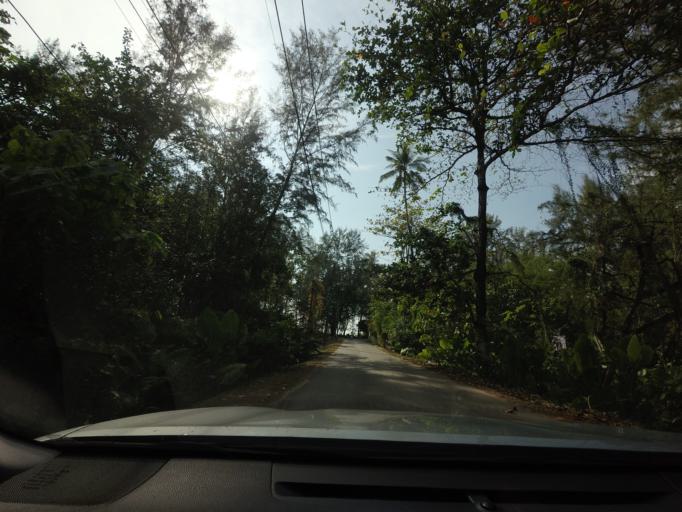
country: TH
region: Phangnga
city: Takua Pa
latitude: 8.7855
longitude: 98.2633
